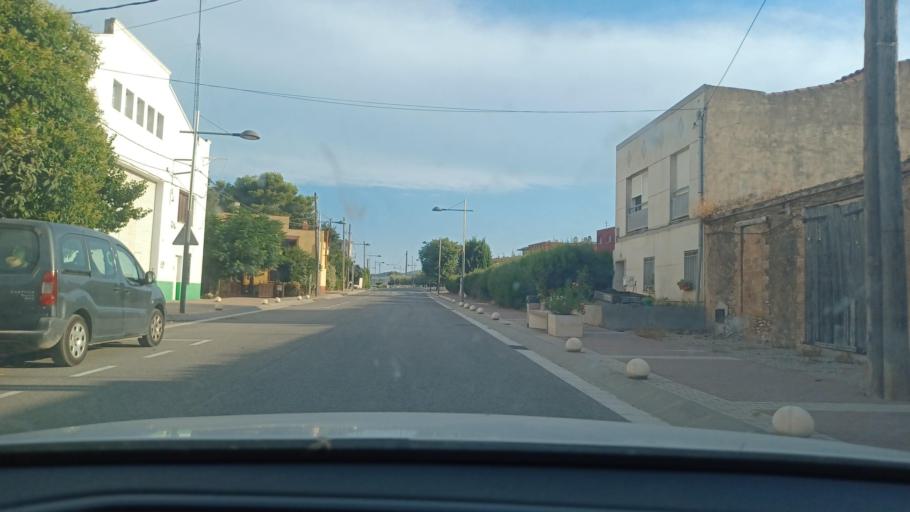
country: ES
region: Catalonia
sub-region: Provincia de Tarragona
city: Santa Barbara
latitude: 40.7146
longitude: 0.5017
